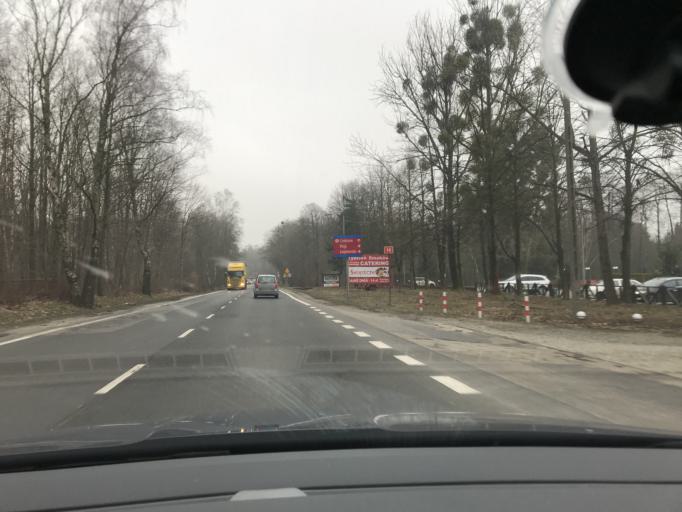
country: PL
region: Lodz Voivodeship
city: Lodz
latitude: 51.8206
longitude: 19.5095
